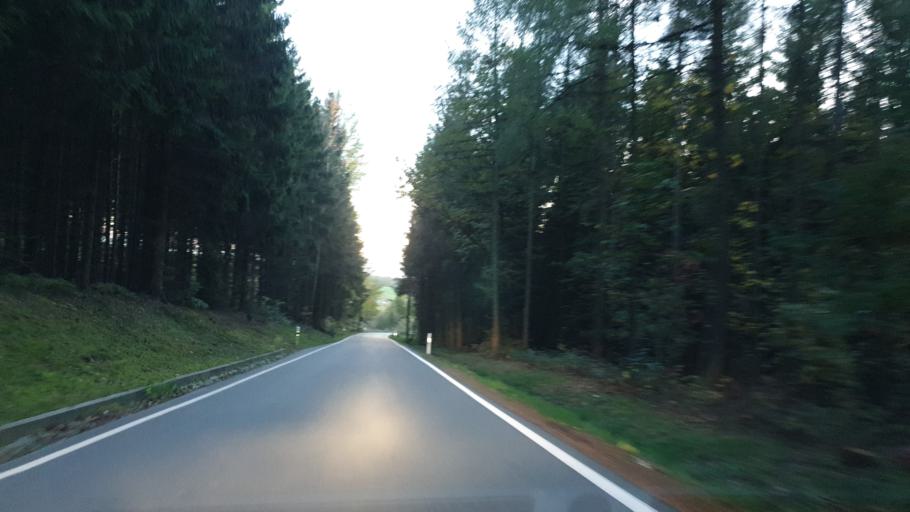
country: DE
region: Saxony
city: Hohndorf
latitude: 50.7128
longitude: 12.6561
